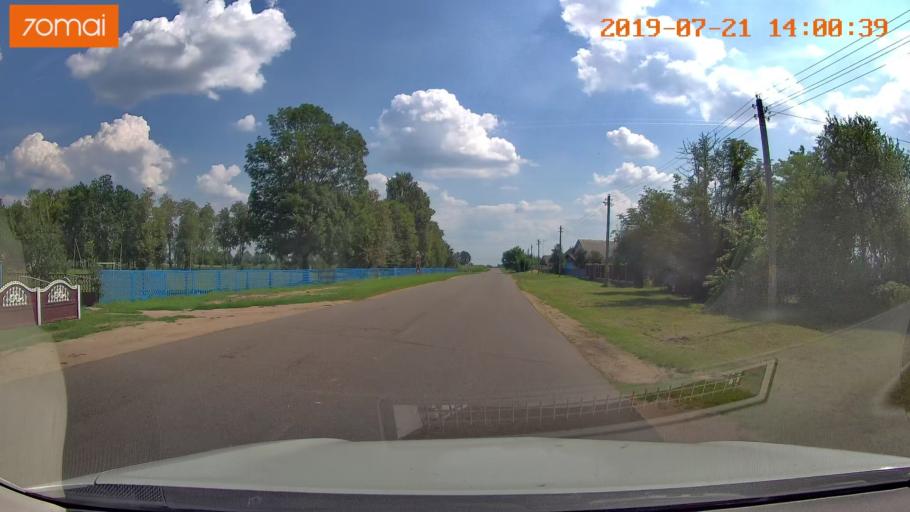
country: BY
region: Grodnenskaya
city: Lyubcha
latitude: 53.7494
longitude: 26.0668
